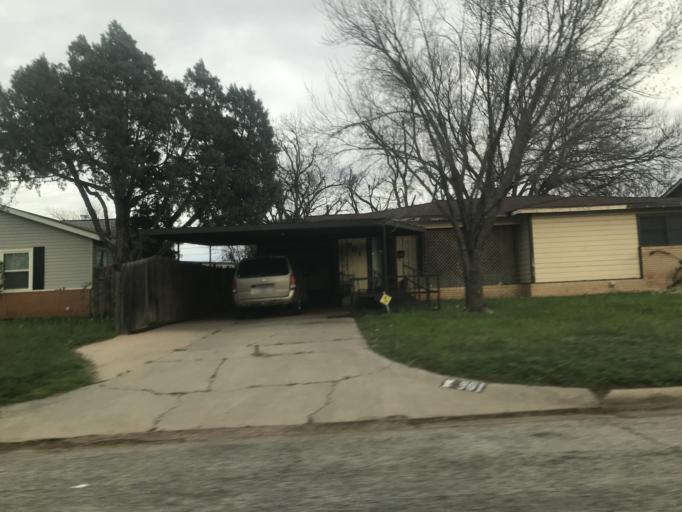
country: US
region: Texas
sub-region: Taylor County
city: Abilene
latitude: 32.4600
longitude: -99.7558
